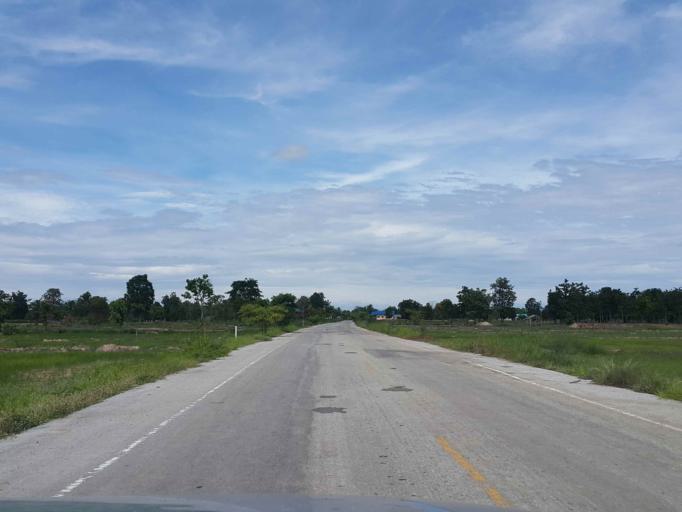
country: TH
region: Sukhothai
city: Ban Dan Lan Hoi
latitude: 17.1094
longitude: 99.4865
